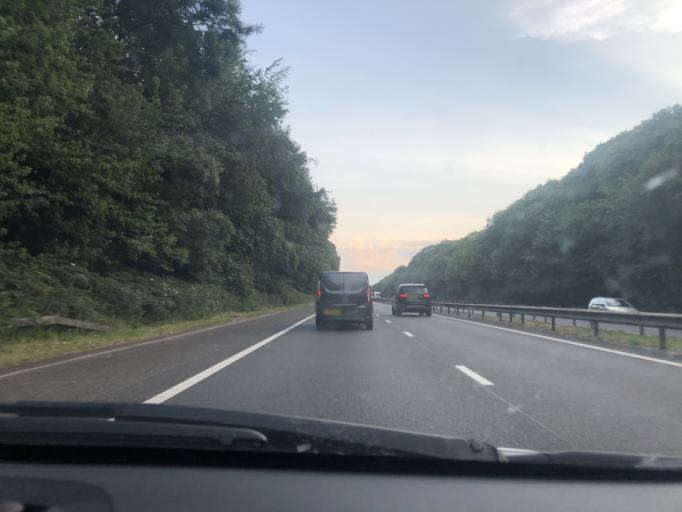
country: GB
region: England
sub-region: Kent
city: Rainham
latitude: 51.3396
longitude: 0.6001
